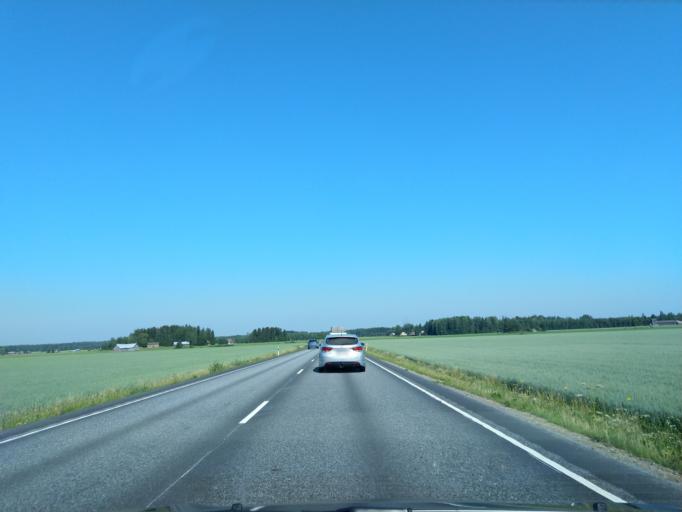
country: FI
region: Varsinais-Suomi
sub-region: Loimaa
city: Alastaro
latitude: 61.0882
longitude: 22.8877
